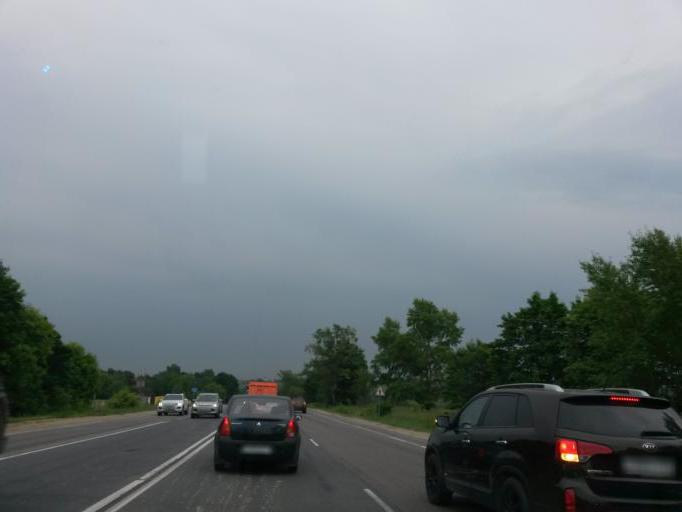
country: RU
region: Moskovskaya
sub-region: Podol'skiy Rayon
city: Podol'sk
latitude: 55.4402
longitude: 37.6359
